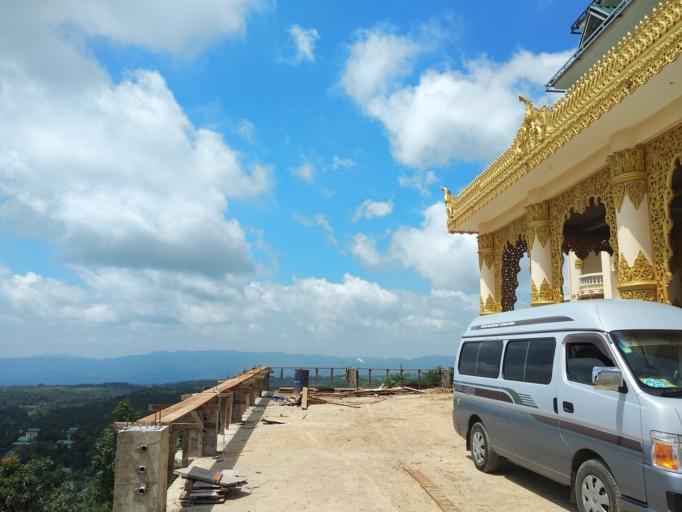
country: MM
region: Mandalay
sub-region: Pyin Oo Lwin District
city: Pyin Oo Lwin
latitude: 21.9092
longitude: 96.3885
